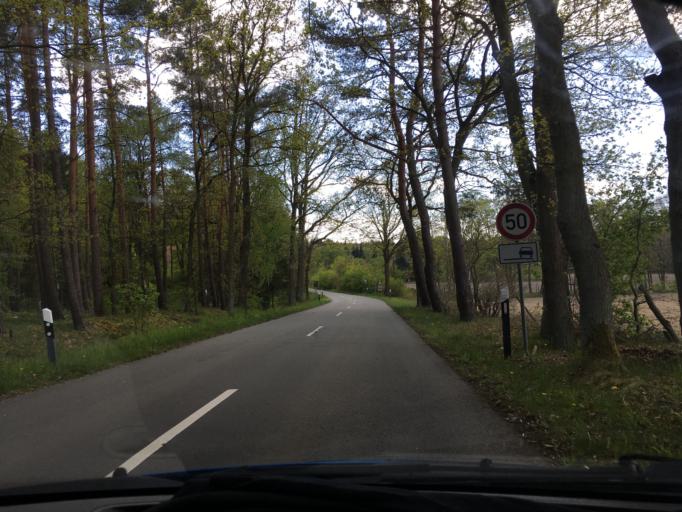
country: DE
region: Lower Saxony
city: Nahrendorf
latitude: 53.1455
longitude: 10.8097
